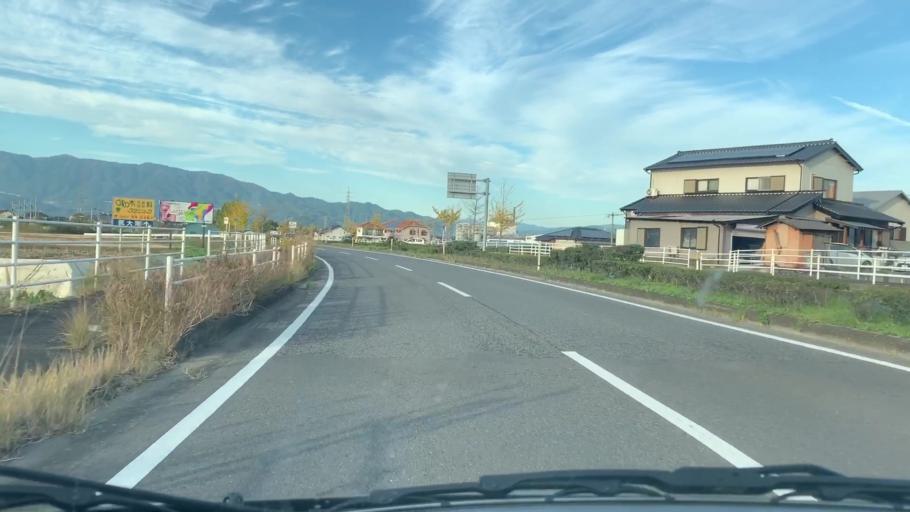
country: JP
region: Saga Prefecture
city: Saga-shi
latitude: 33.2499
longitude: 130.1985
